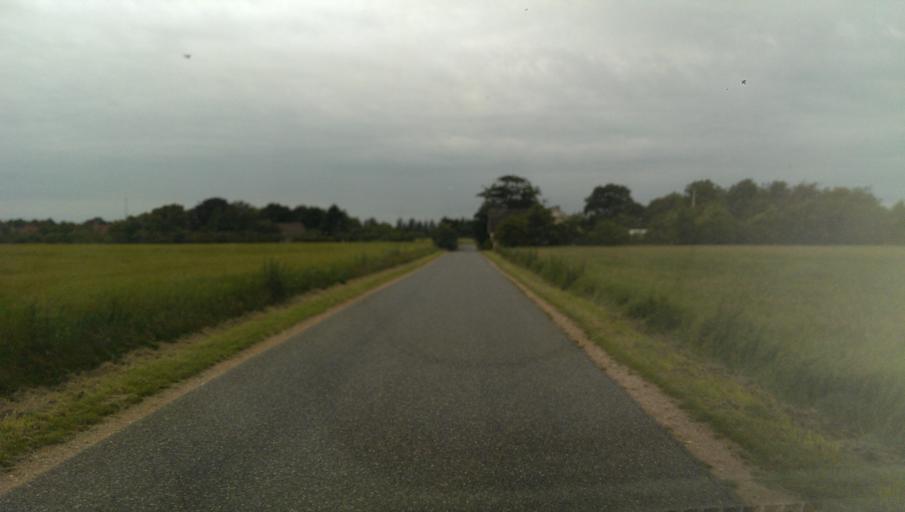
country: DK
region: South Denmark
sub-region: Esbjerg Kommune
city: Bramming
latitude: 55.4789
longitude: 8.7191
